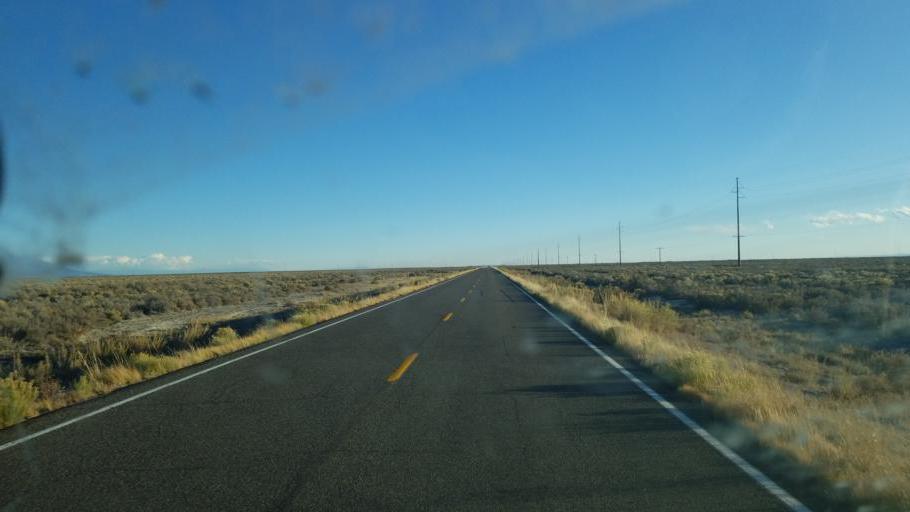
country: US
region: Colorado
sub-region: Saguache County
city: Center
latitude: 37.9311
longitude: -105.9010
